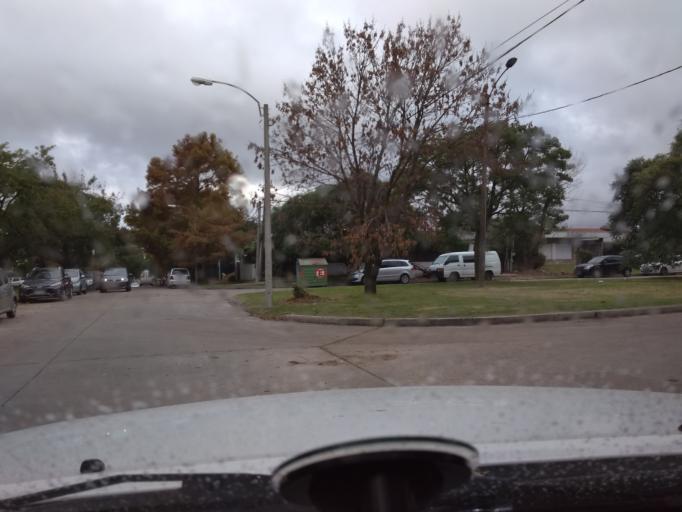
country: UY
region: Canelones
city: Paso de Carrasco
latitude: -34.8834
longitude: -56.0803
